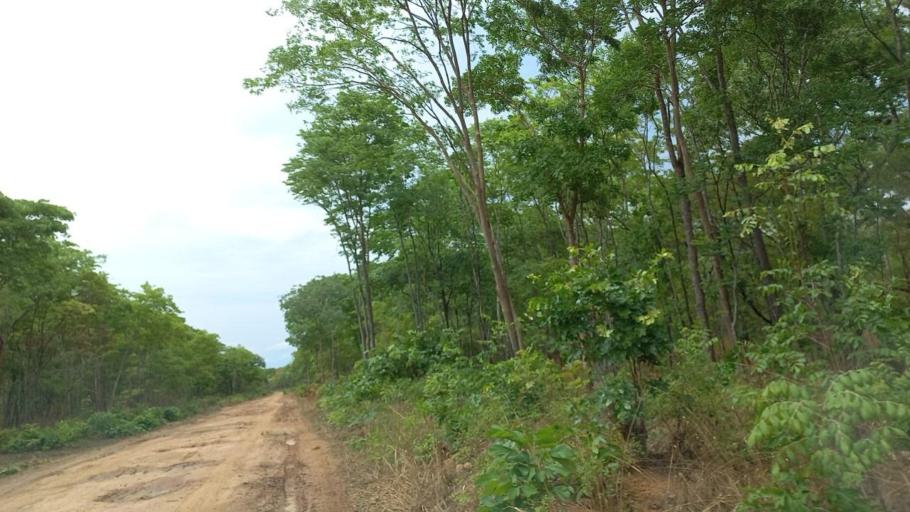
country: ZM
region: North-Western
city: Kalengwa
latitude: -13.5665
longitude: 24.9711
